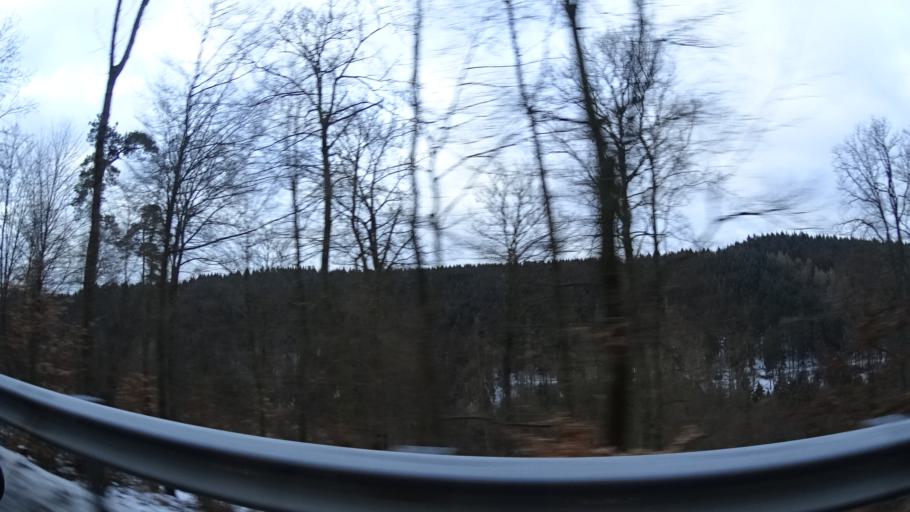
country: DE
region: Baden-Wuerttemberg
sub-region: Karlsruhe Region
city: Zwingenberg
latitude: 49.4485
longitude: 9.0349
